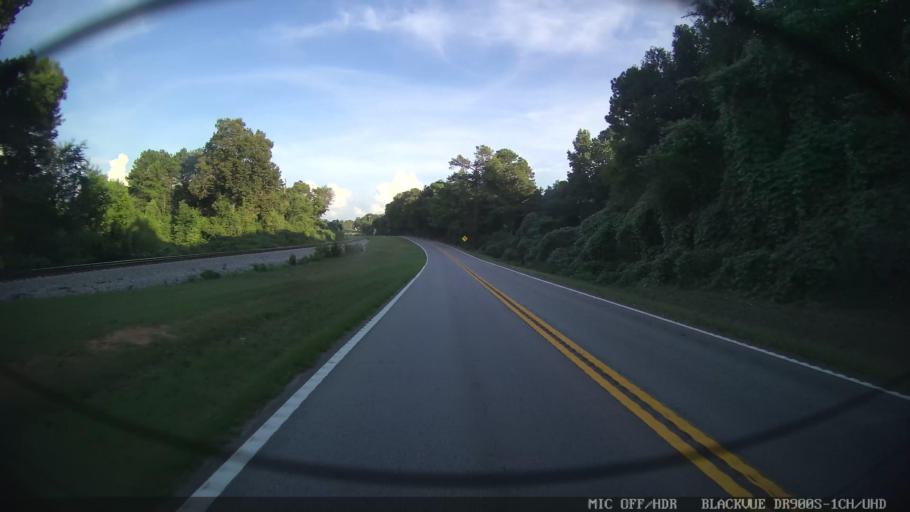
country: US
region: Georgia
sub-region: Monroe County
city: Forsyth
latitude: 32.9487
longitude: -83.8480
